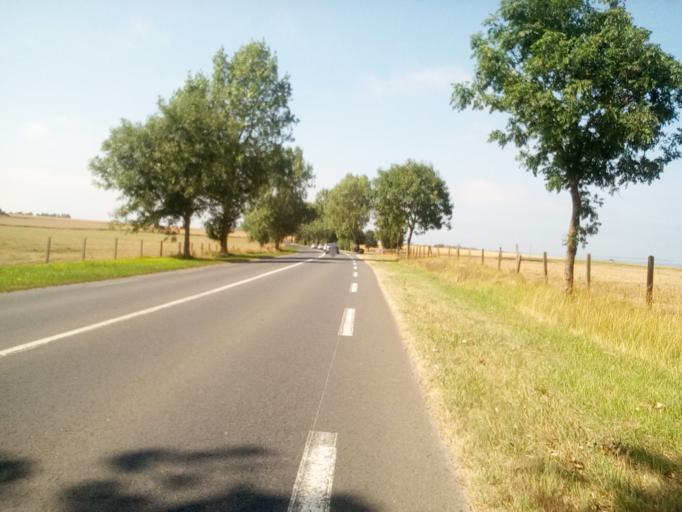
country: FR
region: Lower Normandy
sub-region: Departement du Calvados
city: Bernieres-sur-Mer
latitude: 49.3060
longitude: -0.4387
